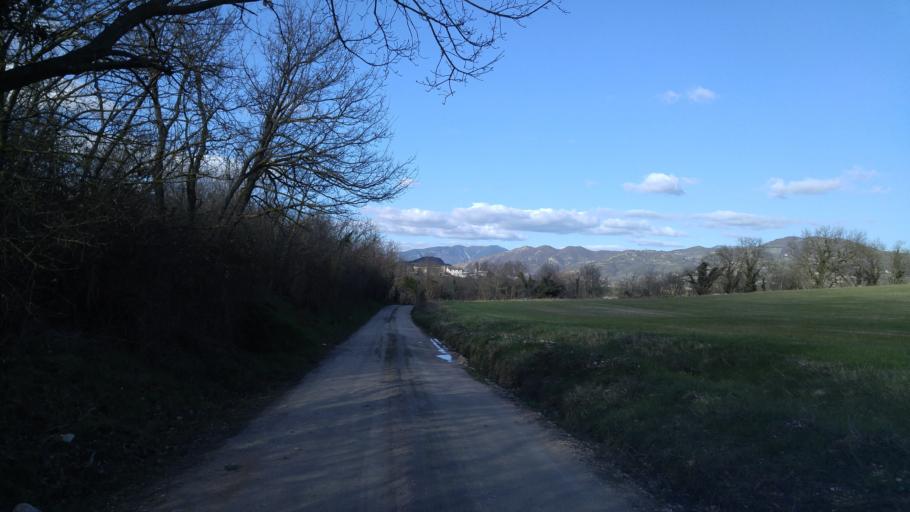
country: IT
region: The Marches
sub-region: Provincia di Pesaro e Urbino
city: Cagli
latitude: 43.5578
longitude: 12.6574
